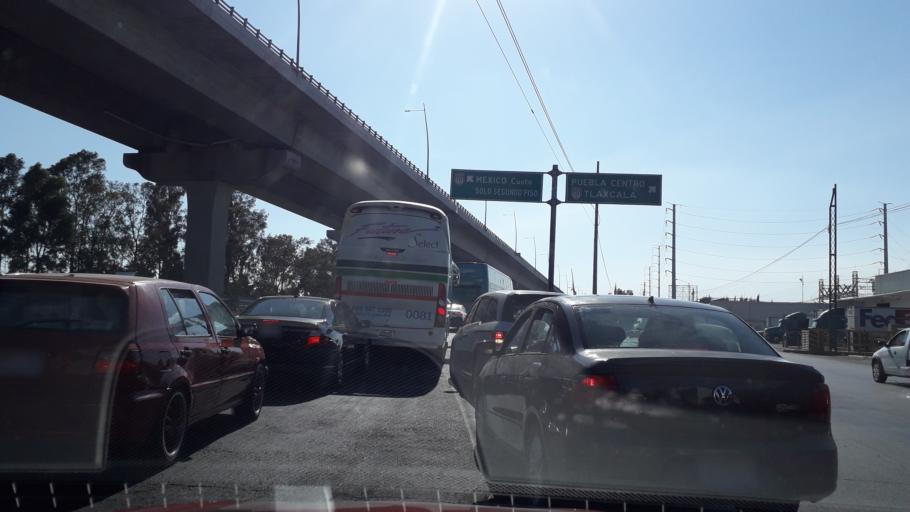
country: MX
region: Puebla
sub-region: Puebla
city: San Sebastian de Aparicio
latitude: 19.0847
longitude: -98.1905
